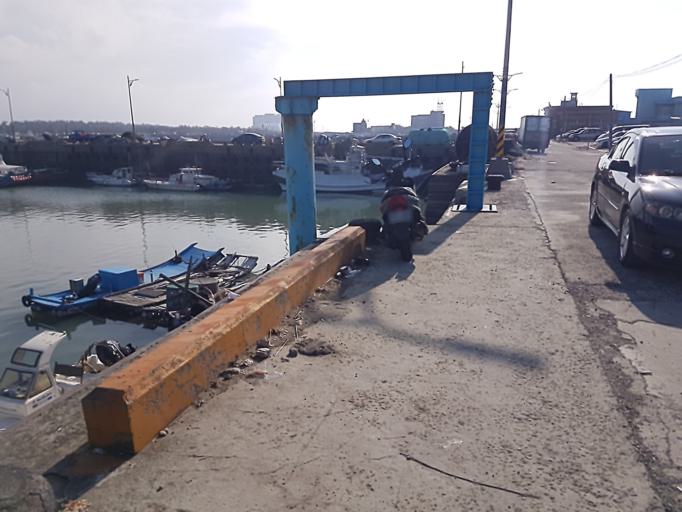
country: TW
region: Taiwan
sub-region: Hsinchu
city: Hsinchu
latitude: 24.8505
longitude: 120.9223
